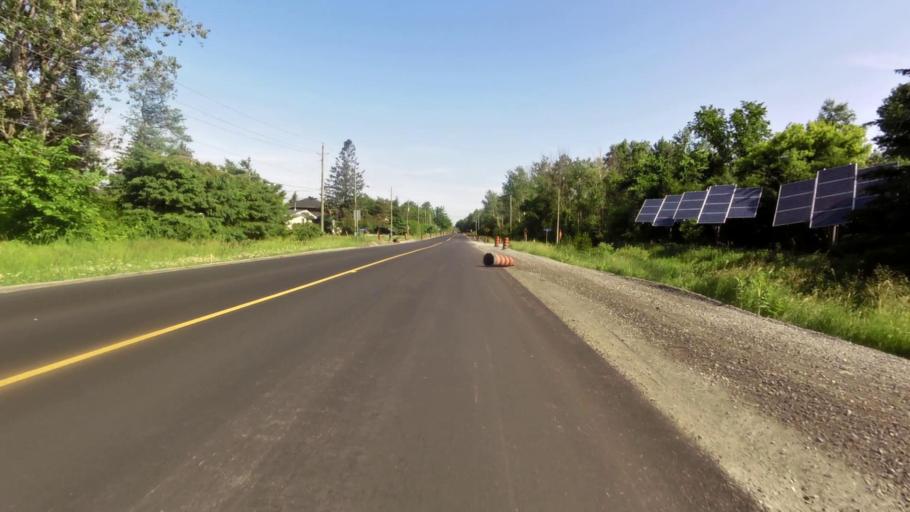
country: CA
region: Ontario
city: Ottawa
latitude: 45.2549
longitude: -75.5930
